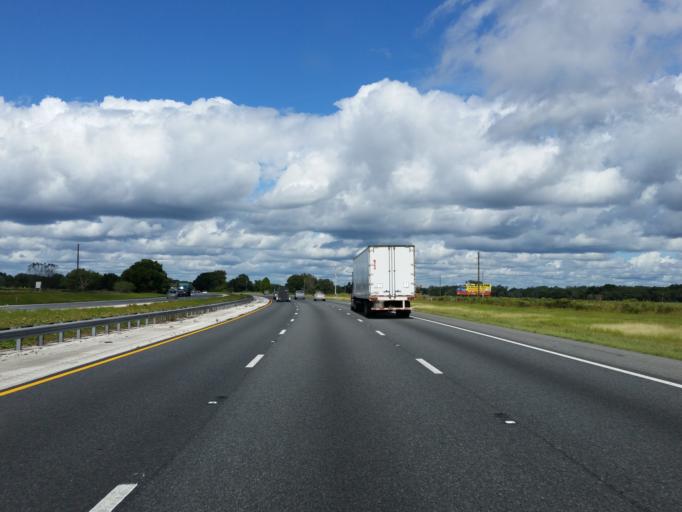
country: US
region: Florida
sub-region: Sumter County
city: Wildwood
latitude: 28.9350
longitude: -82.1119
